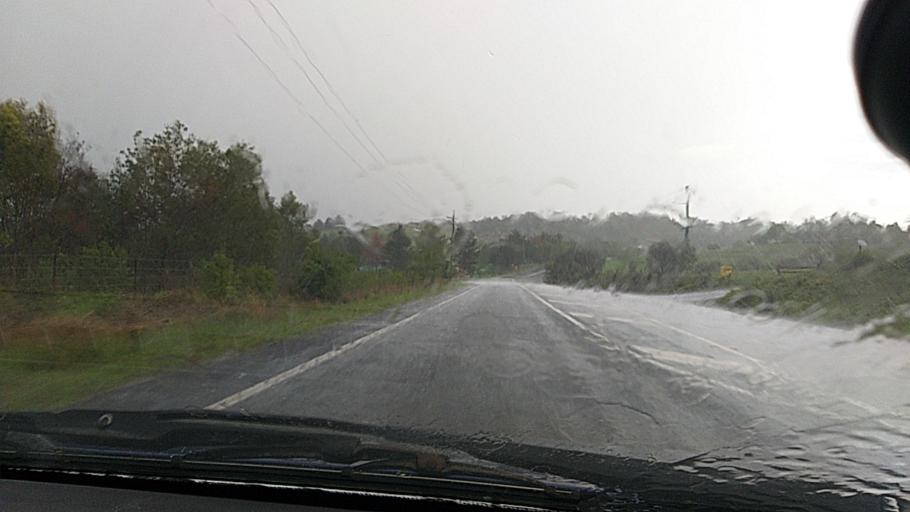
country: AU
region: New South Wales
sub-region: Wollondilly
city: Douglas Park
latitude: -34.1681
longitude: 150.7146
